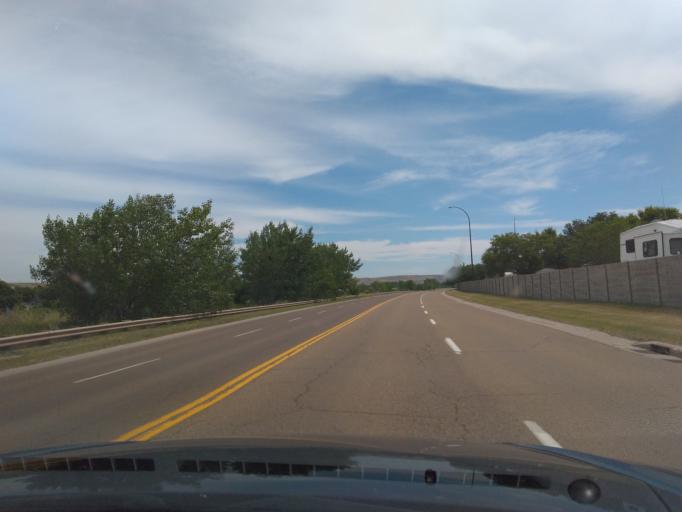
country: CA
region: Alberta
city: Three Hills
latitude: 51.4635
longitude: -112.7448
